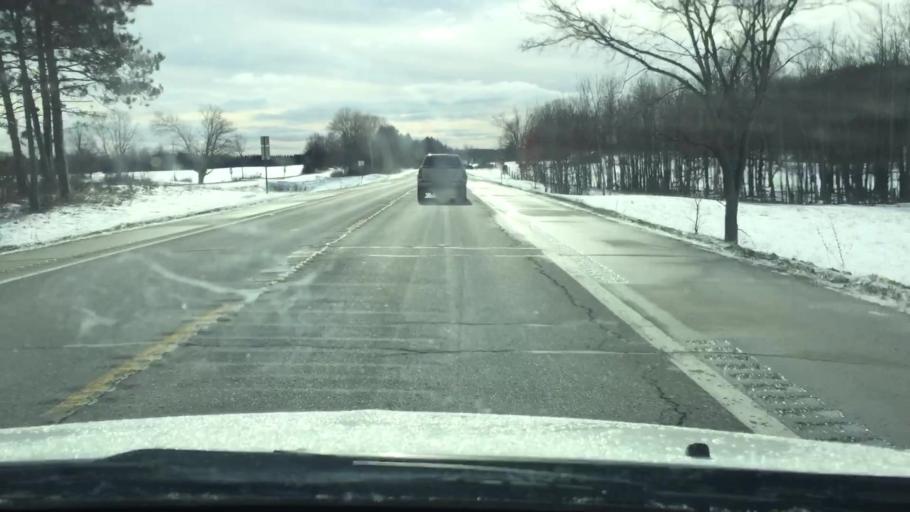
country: US
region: Michigan
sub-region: Wexford County
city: Manton
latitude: 44.5968
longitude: -85.3320
